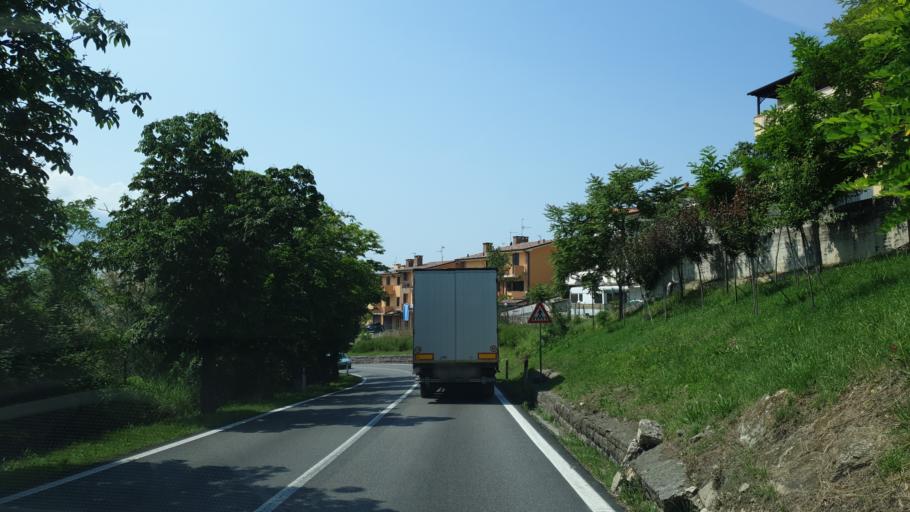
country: SM
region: Acquaviva
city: Acquaviva
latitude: 43.9469
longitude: 12.4185
